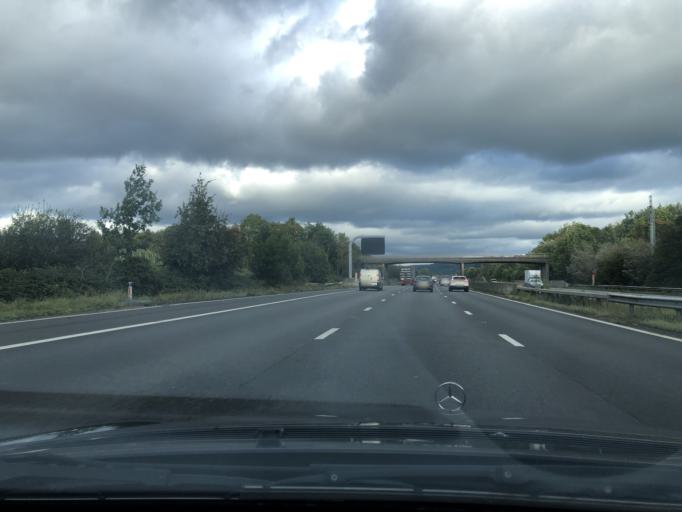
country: GB
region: England
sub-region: Gloucestershire
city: Stonehouse
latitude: 51.8022
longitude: -2.2792
